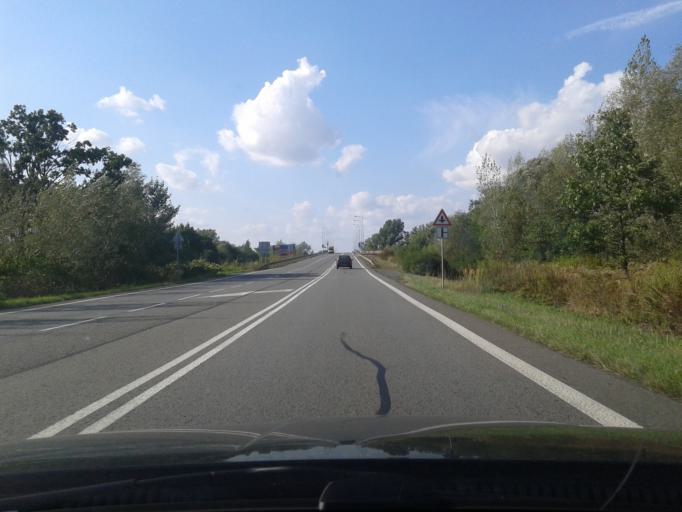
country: CZ
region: Moravskoslezsky
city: Stary Bohumin
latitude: 49.9140
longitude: 18.3274
